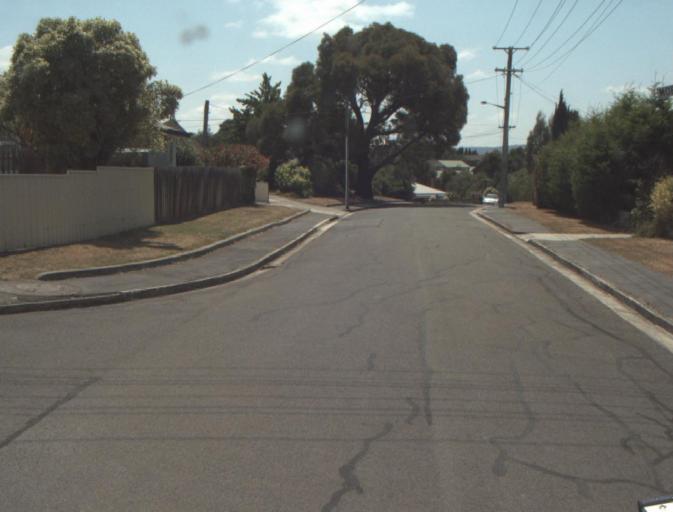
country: AU
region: Tasmania
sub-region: Launceston
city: Newstead
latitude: -41.4670
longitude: 147.1801
